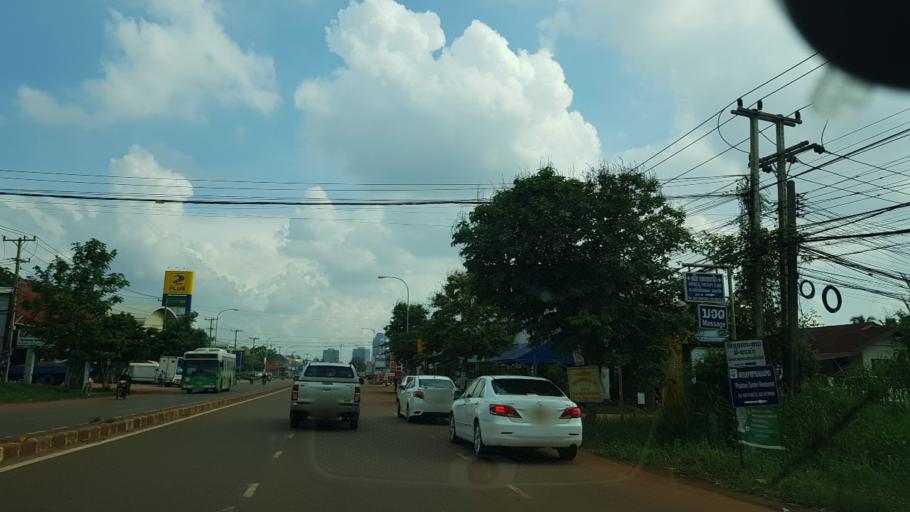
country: LA
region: Vientiane
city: Vientiane
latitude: 18.0188
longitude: 102.6508
